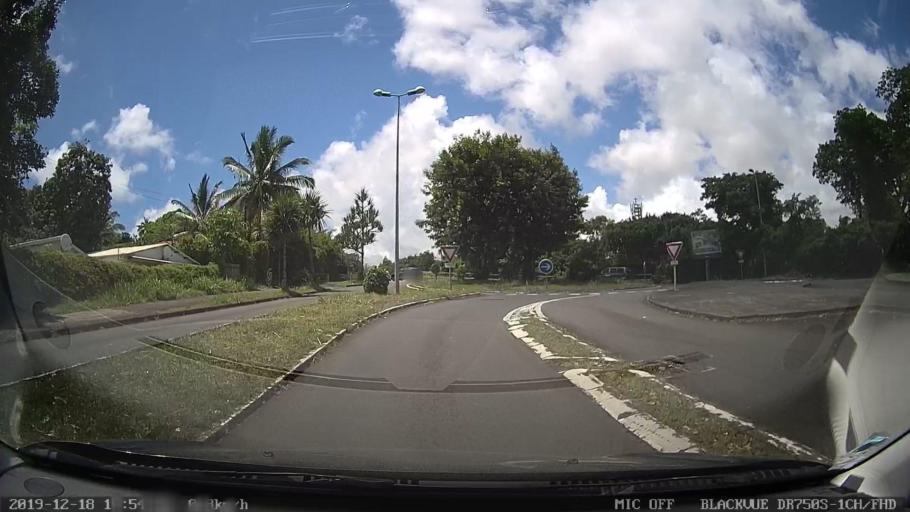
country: RE
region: Reunion
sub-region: Reunion
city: Saint-Andre
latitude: -20.9345
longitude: 55.6379
